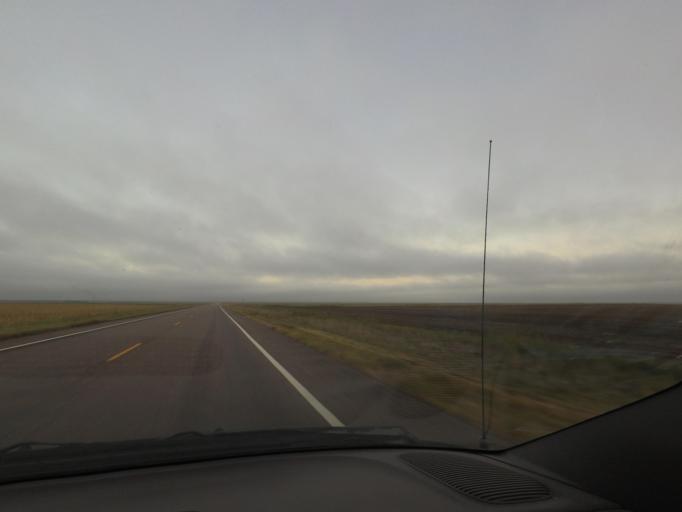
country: US
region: Kansas
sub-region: Cheyenne County
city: Saint Francis
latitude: 39.7463
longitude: -102.1035
